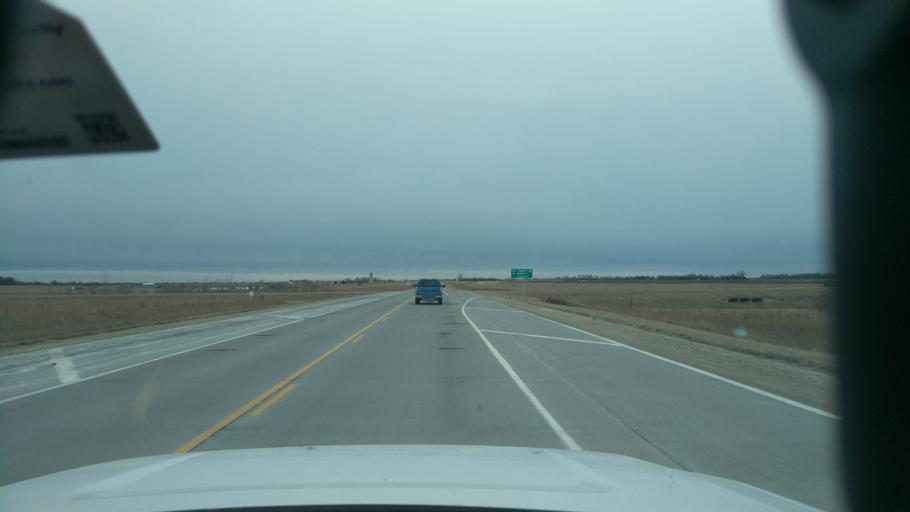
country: US
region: Kansas
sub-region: Dickinson County
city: Herington
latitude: 38.5678
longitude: -96.9501
